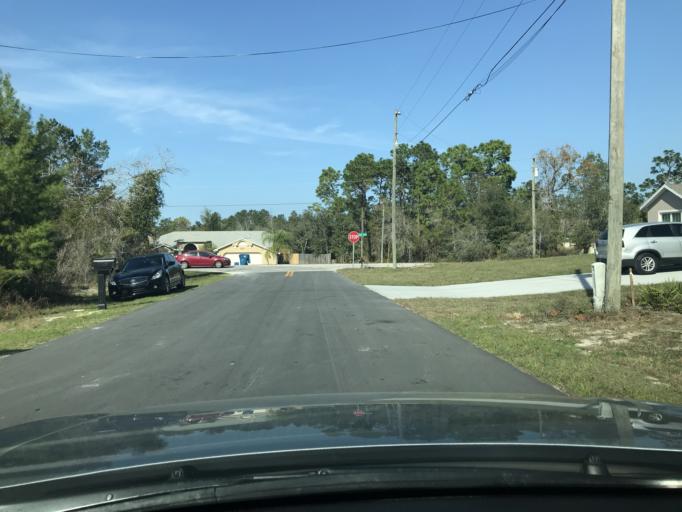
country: US
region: Florida
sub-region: Hernando County
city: North Weeki Wachee
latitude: 28.5470
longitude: -82.5503
